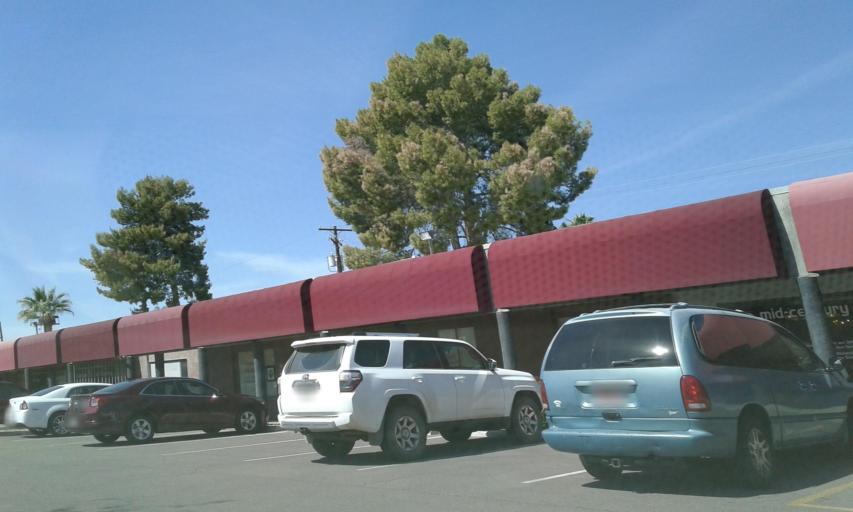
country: US
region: Arizona
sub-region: Maricopa County
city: Phoenix
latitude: 33.5036
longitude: -112.0836
